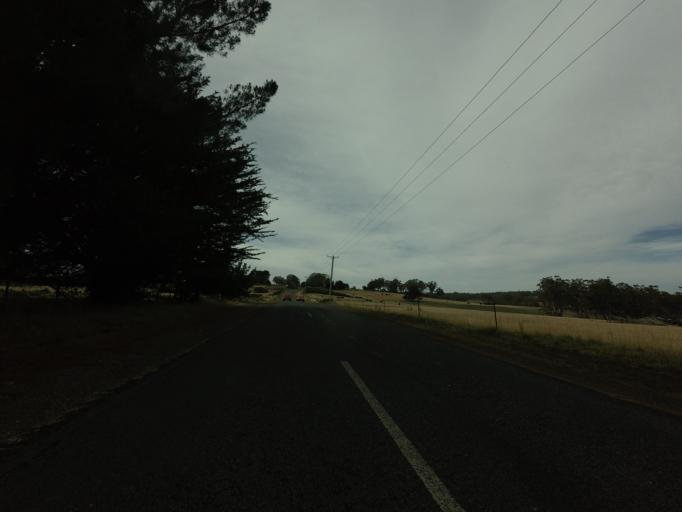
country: AU
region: Tasmania
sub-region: Brighton
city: Bridgewater
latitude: -42.3923
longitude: 147.4311
